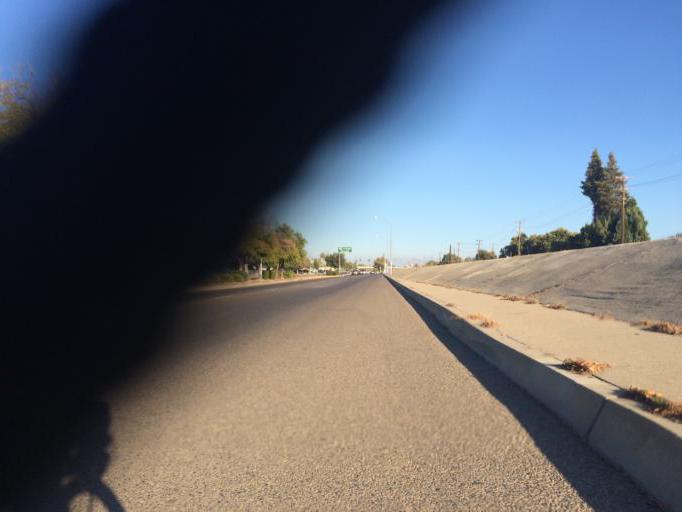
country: US
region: California
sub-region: Fresno County
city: Fresno
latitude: 36.7650
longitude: -119.7577
